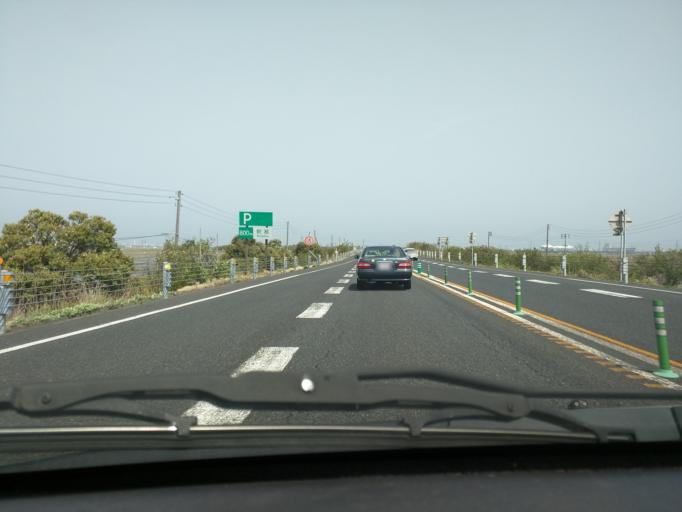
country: JP
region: Niigata
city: Kameda-honcho
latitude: 37.8407
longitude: 139.0670
